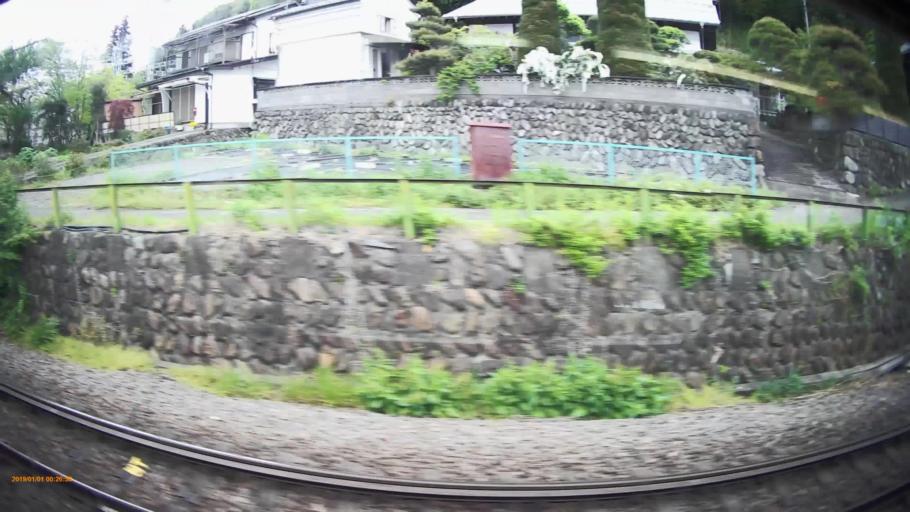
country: JP
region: Yamanashi
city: Uenohara
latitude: 35.6179
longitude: 139.1131
